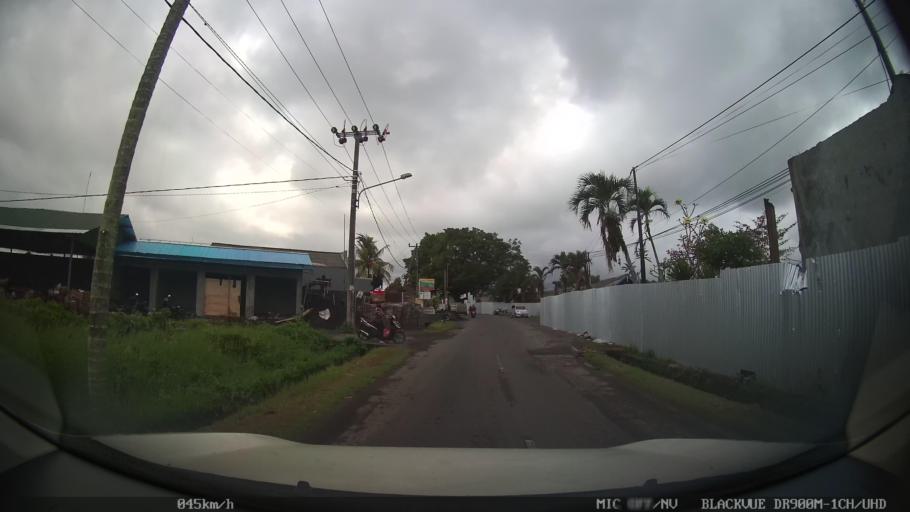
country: ID
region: Bali
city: Banjar Mambalkajanan
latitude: -8.5457
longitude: 115.2133
